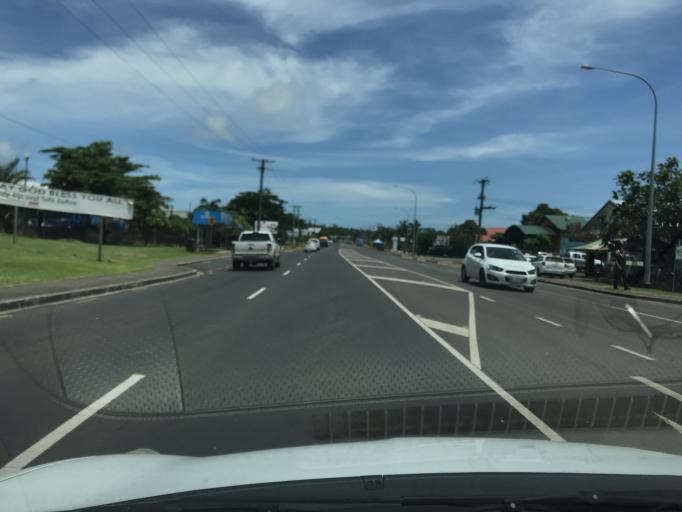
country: WS
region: Tuamasaga
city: Vaiusu
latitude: -13.8213
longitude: -171.8024
